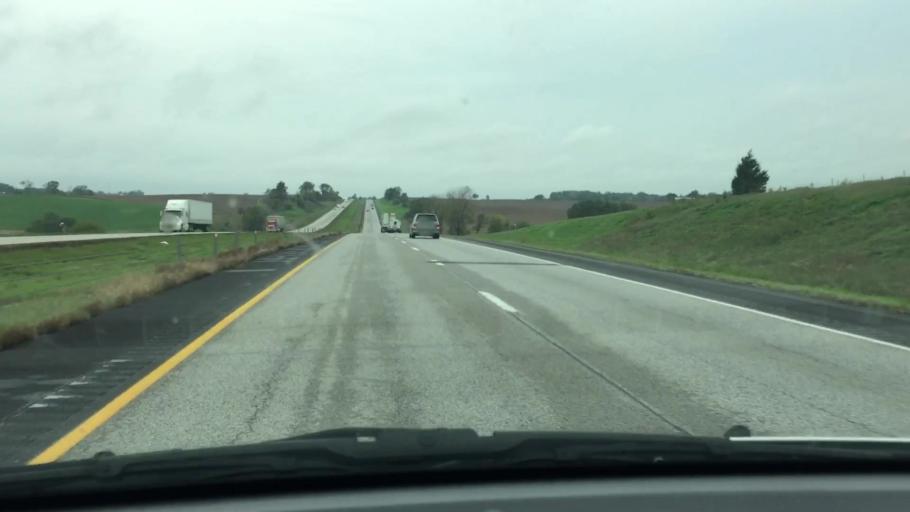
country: US
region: Iowa
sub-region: Johnson County
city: Tiffin
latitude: 41.6953
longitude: -91.7200
